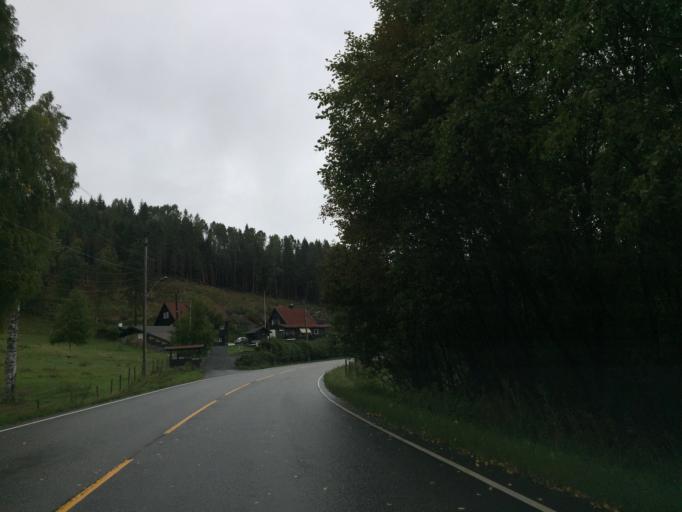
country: NO
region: Akershus
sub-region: Baerum
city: Lysaker
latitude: 59.9949
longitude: 10.6205
